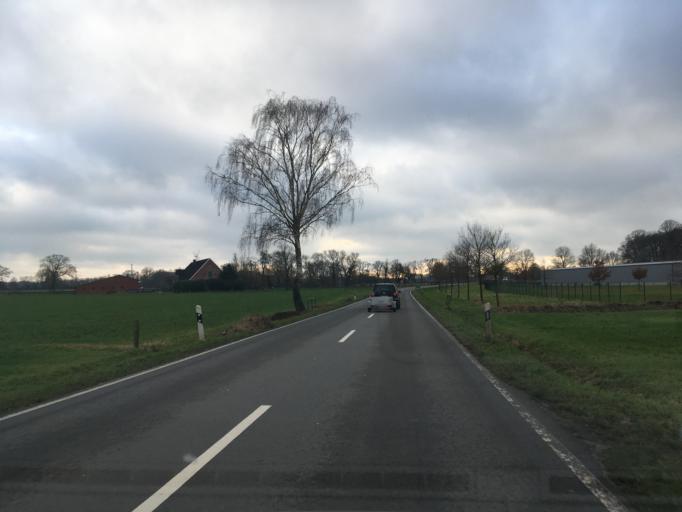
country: DE
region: North Rhine-Westphalia
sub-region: Regierungsbezirk Munster
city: Velen
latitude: 51.9420
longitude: 6.9551
